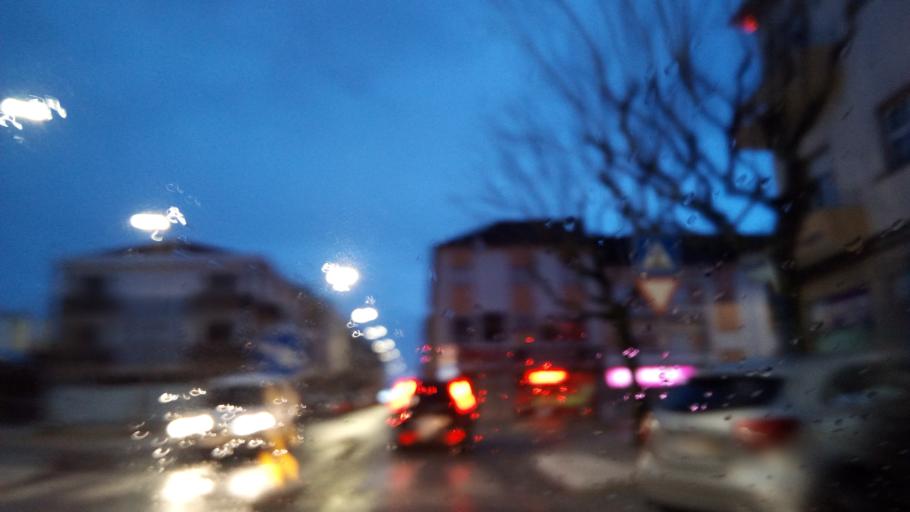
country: PT
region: Viseu
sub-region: Viseu
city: Viseu
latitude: 40.6543
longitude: -7.9144
